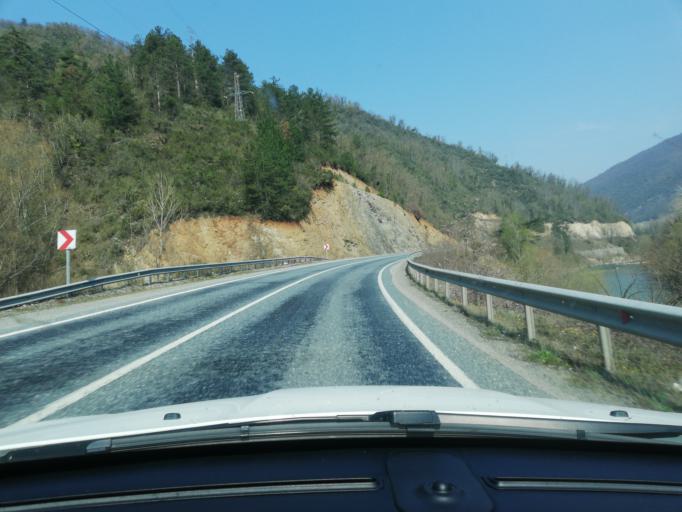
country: TR
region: Zonguldak
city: Gokcebey
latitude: 41.2477
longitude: 32.1683
